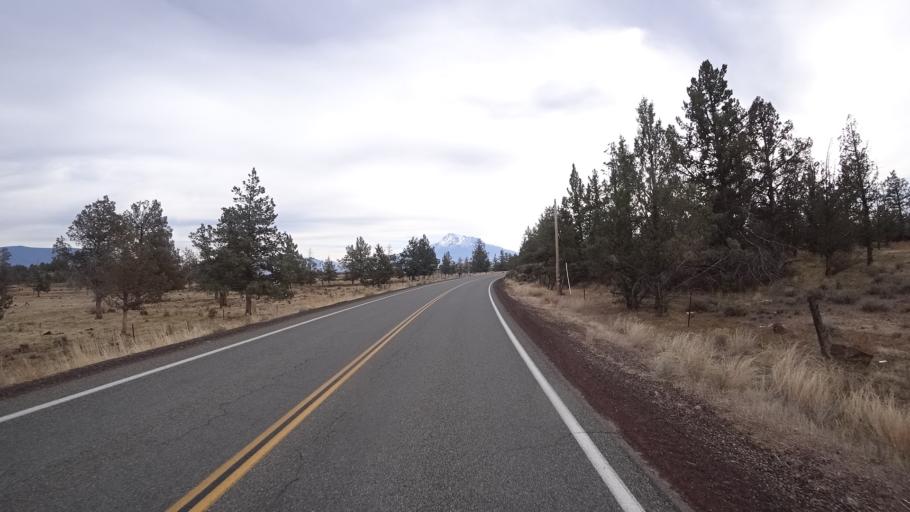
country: US
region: California
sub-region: Siskiyou County
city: Montague
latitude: 41.6331
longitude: -122.4354
